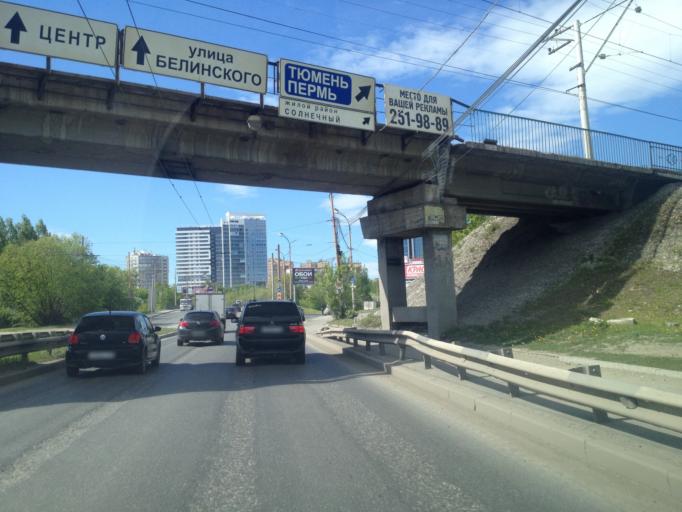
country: RU
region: Sverdlovsk
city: Yekaterinburg
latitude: 56.7936
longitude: 60.6420
